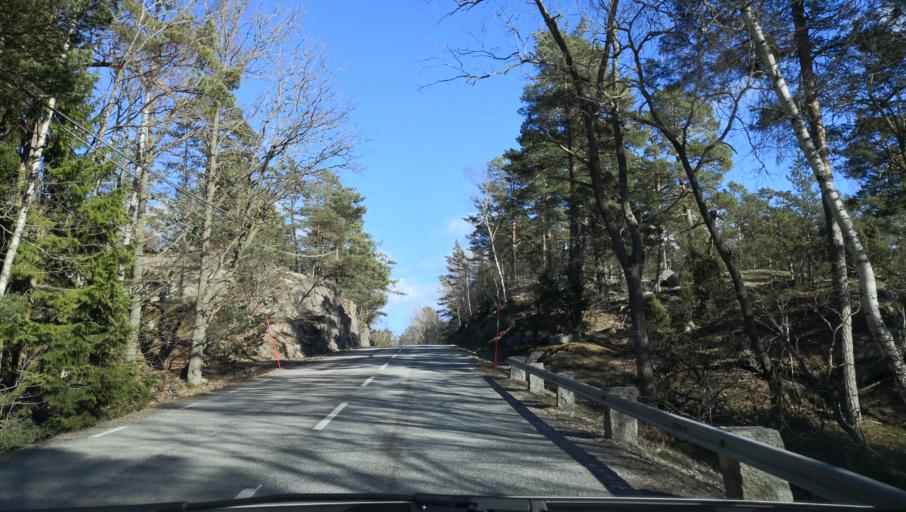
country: SE
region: Stockholm
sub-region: Varmdo Kommun
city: Holo
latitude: 59.3557
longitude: 18.6270
